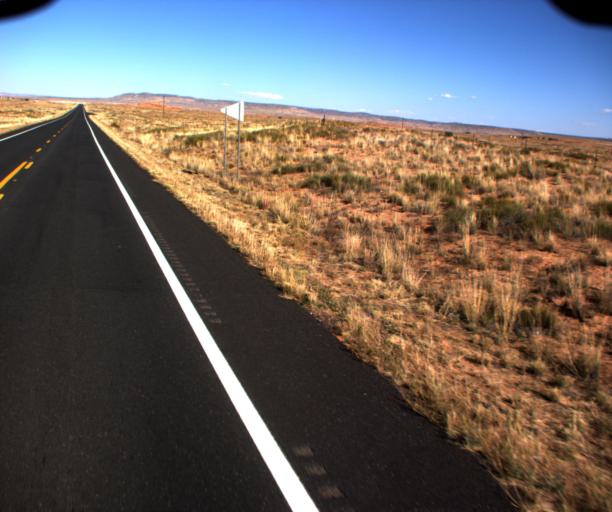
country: US
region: Arizona
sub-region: Coconino County
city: Tuba City
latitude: 36.2976
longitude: -110.9811
